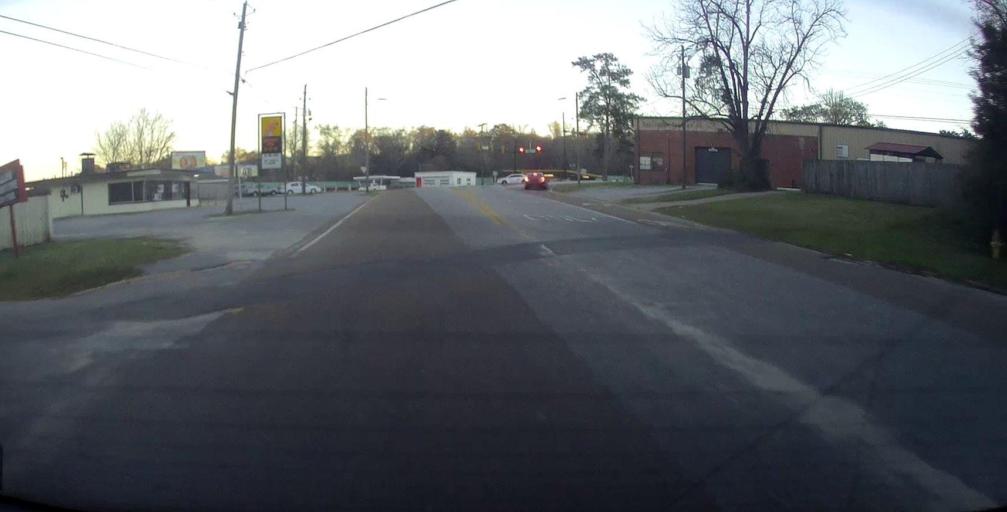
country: US
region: Alabama
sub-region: Russell County
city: Phenix City
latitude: 32.4755
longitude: -85.0247
